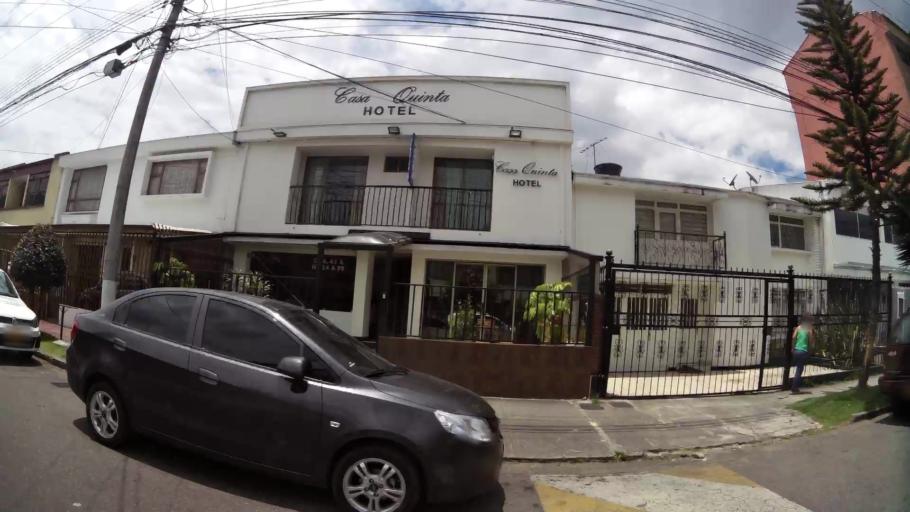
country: CO
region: Bogota D.C.
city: Bogota
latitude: 4.6332
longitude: -74.0924
